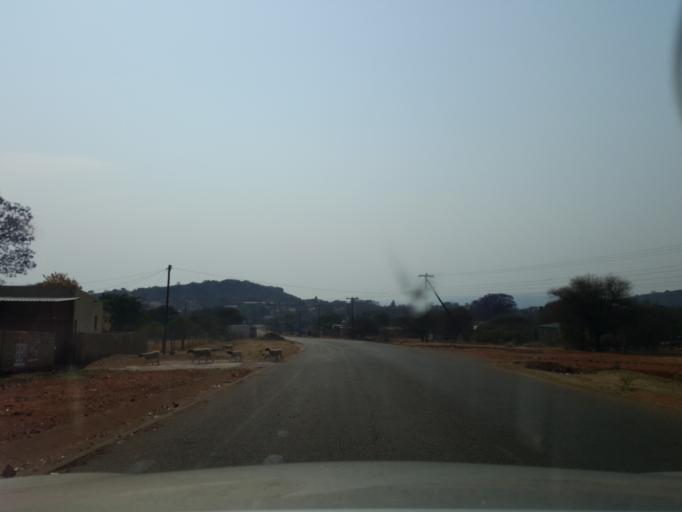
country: BW
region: South East
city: Lobatse
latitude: -25.2847
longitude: 25.8806
